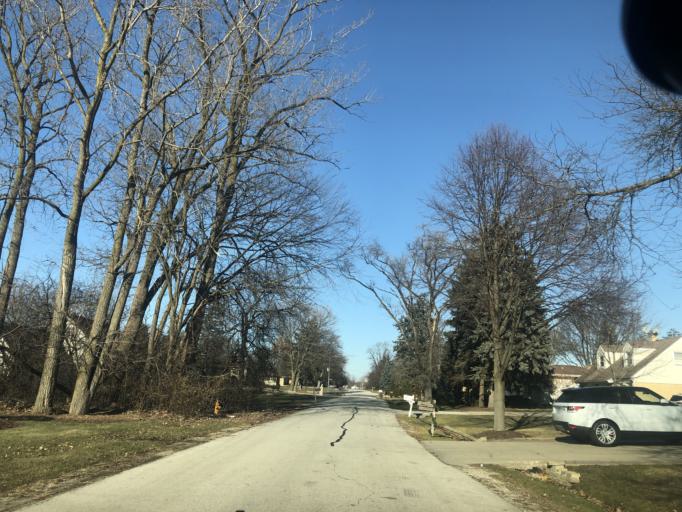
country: US
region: Illinois
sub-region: DuPage County
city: Addison
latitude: 41.9364
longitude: -88.0104
